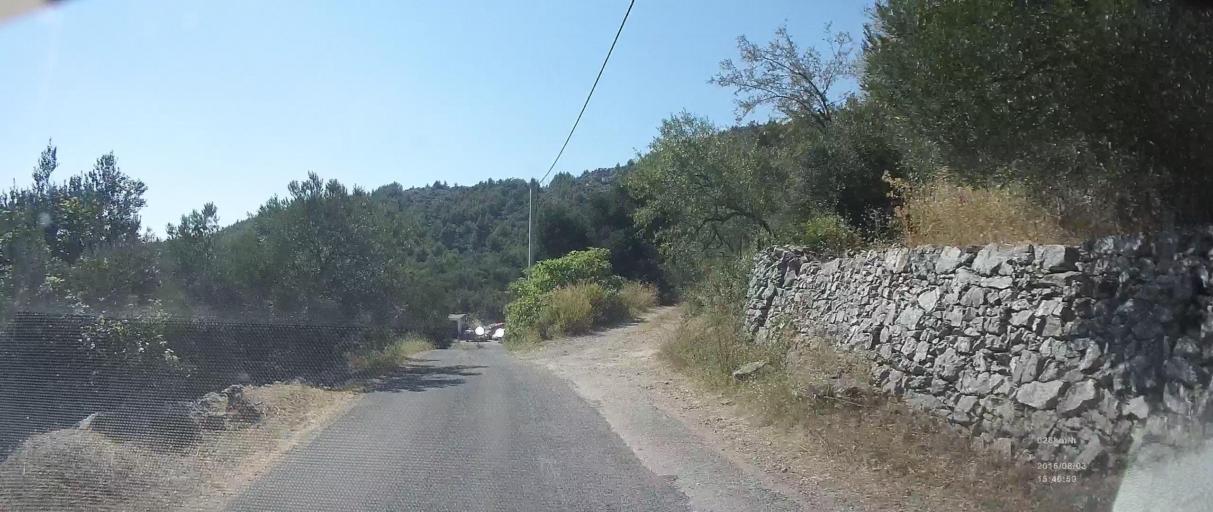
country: HR
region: Dubrovacko-Neretvanska
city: Blato
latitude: 42.7395
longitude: 17.5379
